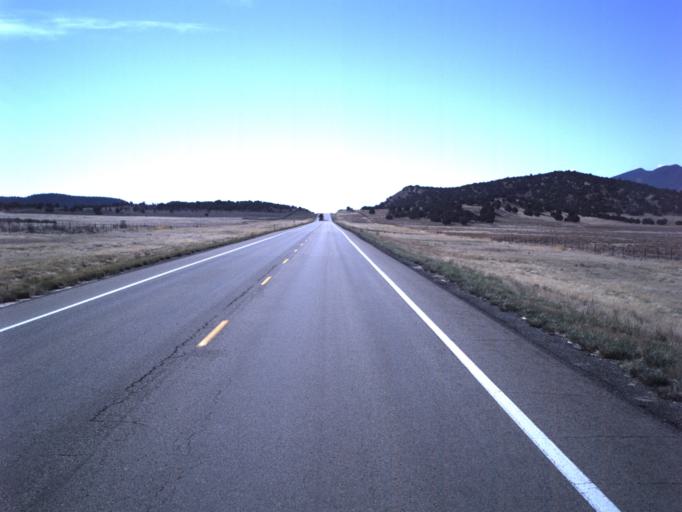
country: US
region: Utah
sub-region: Sanpete County
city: Gunnison
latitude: 39.3981
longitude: -111.9279
